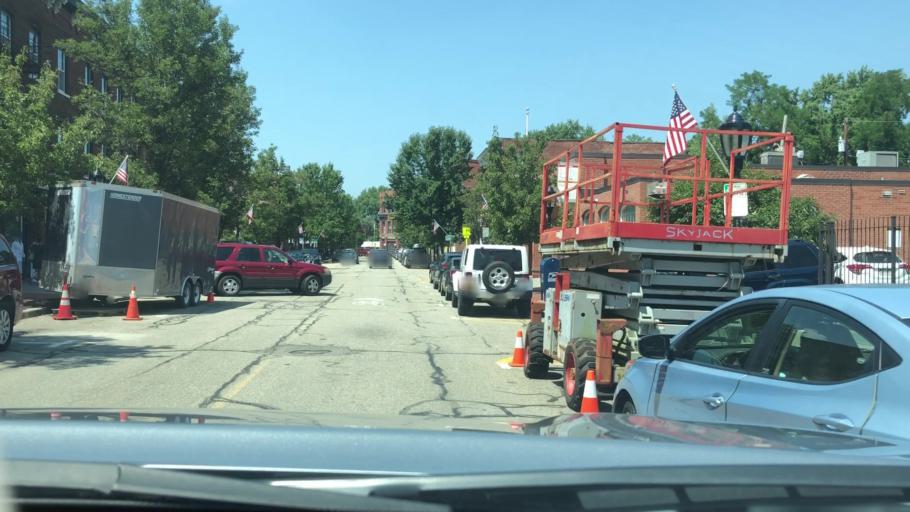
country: US
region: New York
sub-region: Dutchess County
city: Beacon
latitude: 41.5073
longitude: -73.9739
